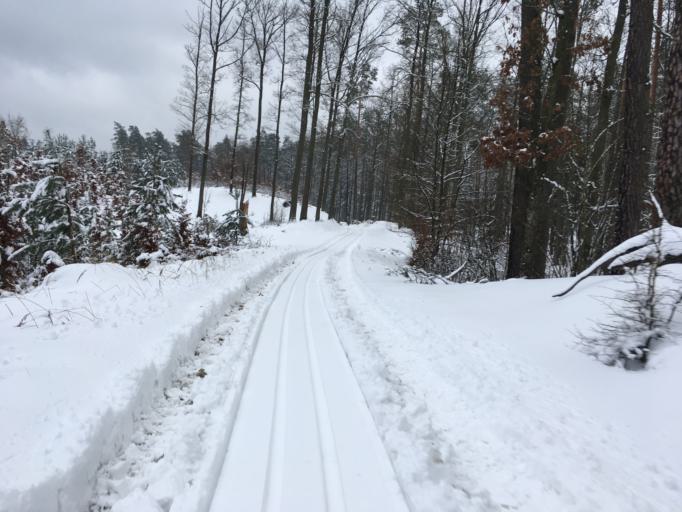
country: PL
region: Kujawsko-Pomorskie
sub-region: Powiat brodnicki
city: Gorzno
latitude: 53.1970
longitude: 19.6759
